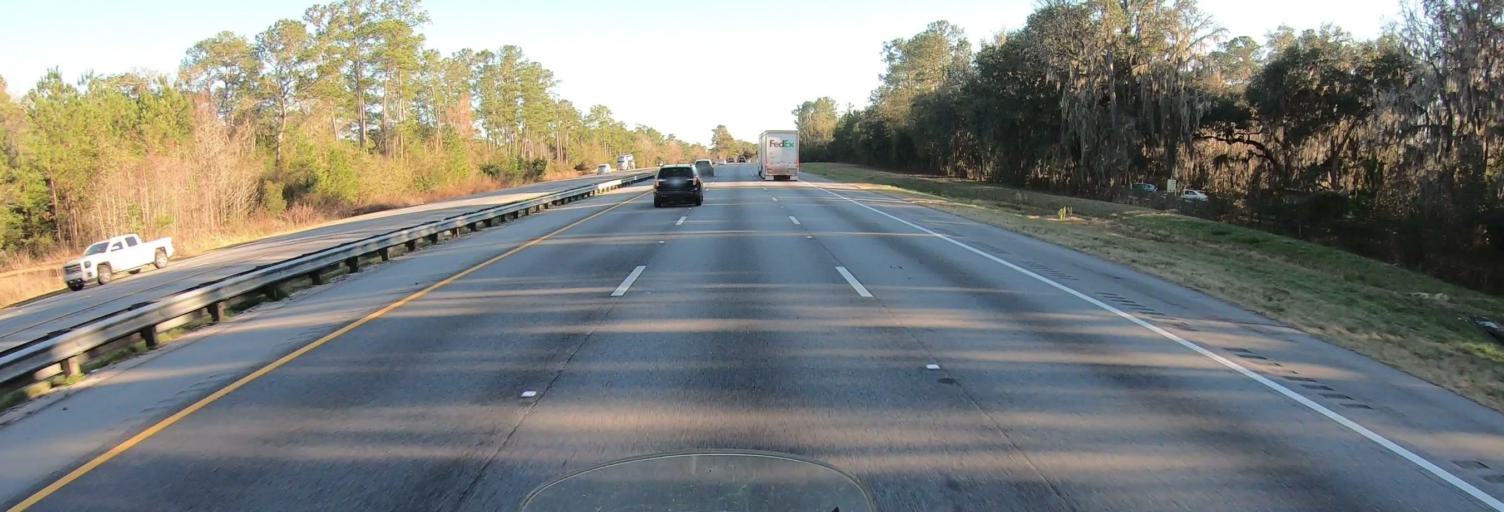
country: US
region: Florida
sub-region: Alachua County
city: Gainesville
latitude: 29.5163
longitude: -82.3059
